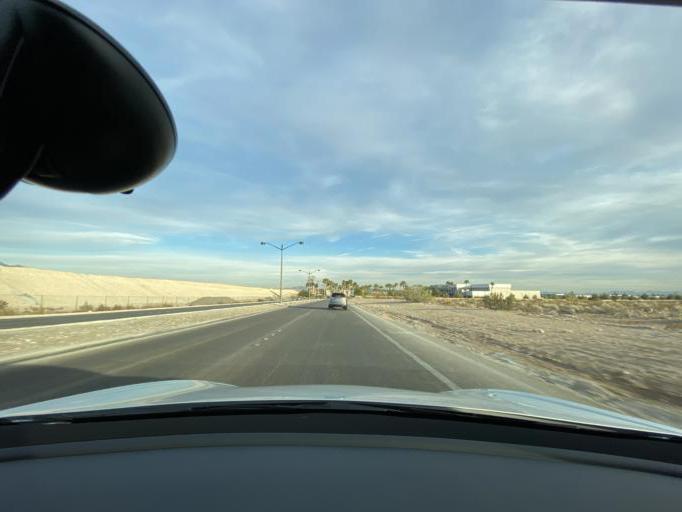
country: US
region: Nevada
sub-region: Clark County
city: Summerlin South
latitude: 36.2771
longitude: -115.2761
